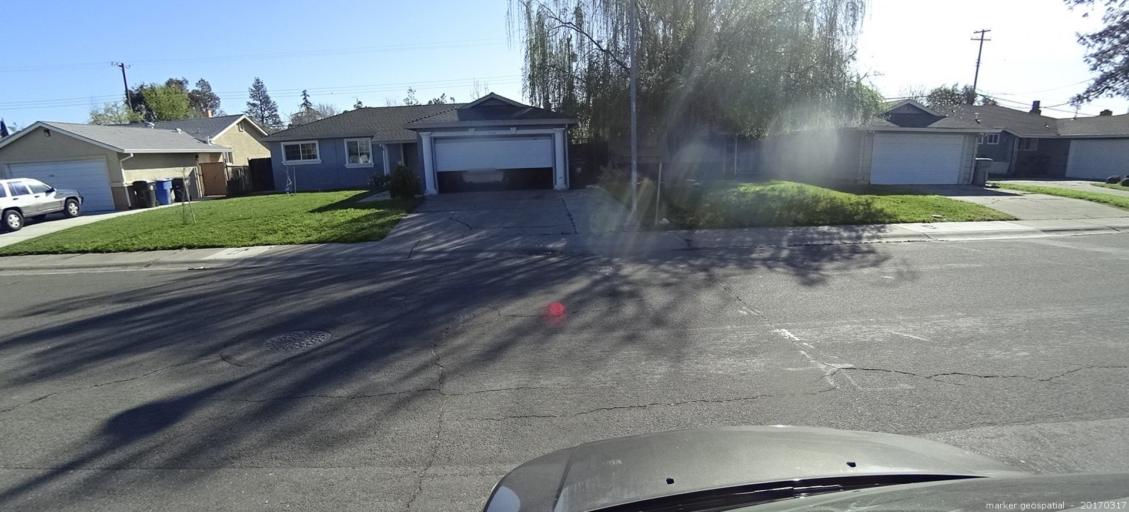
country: US
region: California
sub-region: Sacramento County
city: Parkway
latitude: 38.4827
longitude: -121.4989
